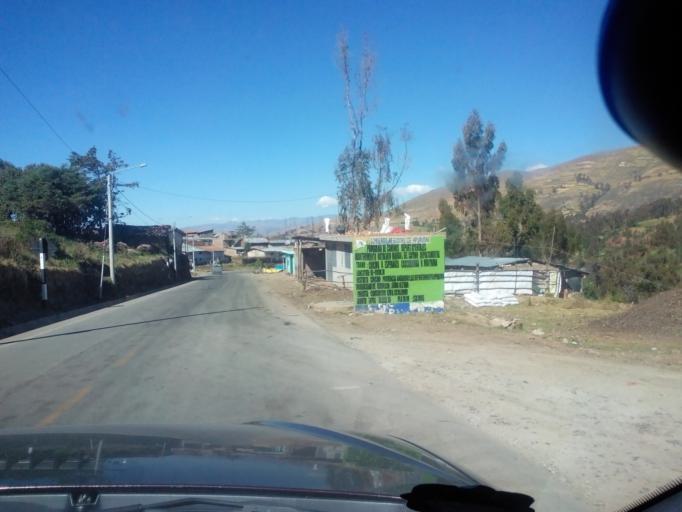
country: PE
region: Apurimac
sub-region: Provincia de Andahuaylas
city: Huancaray
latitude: -13.6529
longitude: -73.5360
